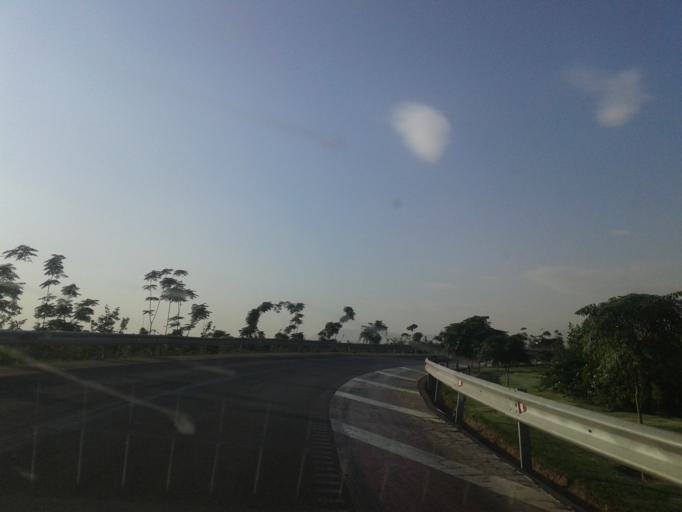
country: IR
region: Tehran
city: Eslamshahr
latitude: 35.6485
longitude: 51.2735
